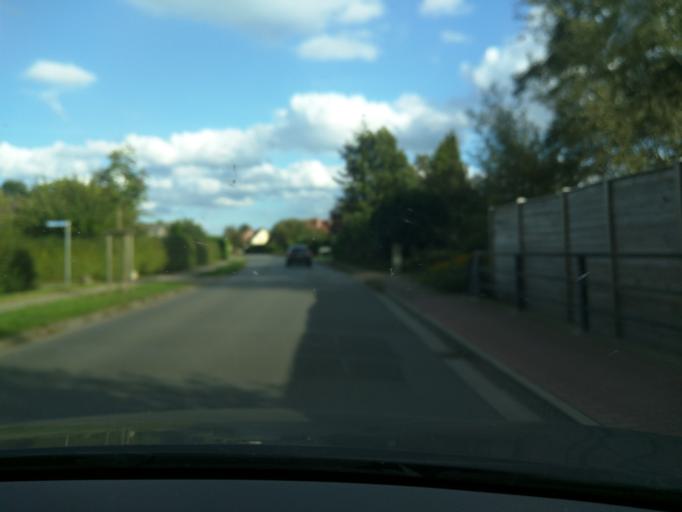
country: DE
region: Lower Saxony
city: Marschacht
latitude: 53.4096
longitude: 10.3900
